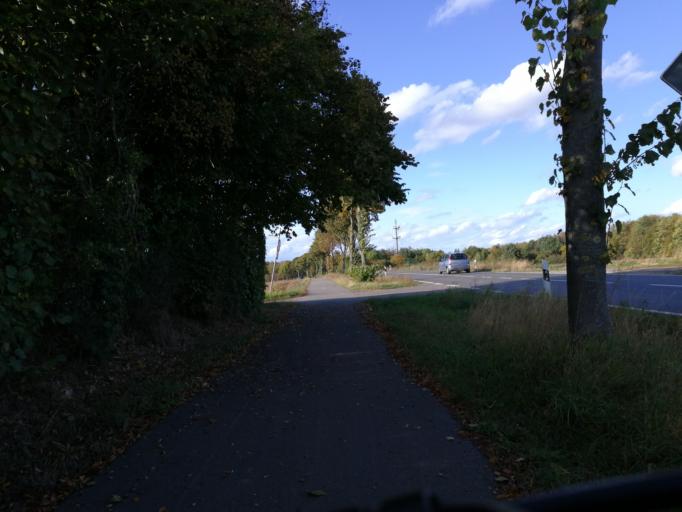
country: DE
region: North Rhine-Westphalia
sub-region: Regierungsbezirk Dusseldorf
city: Neubrueck
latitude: 51.1130
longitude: 6.7143
